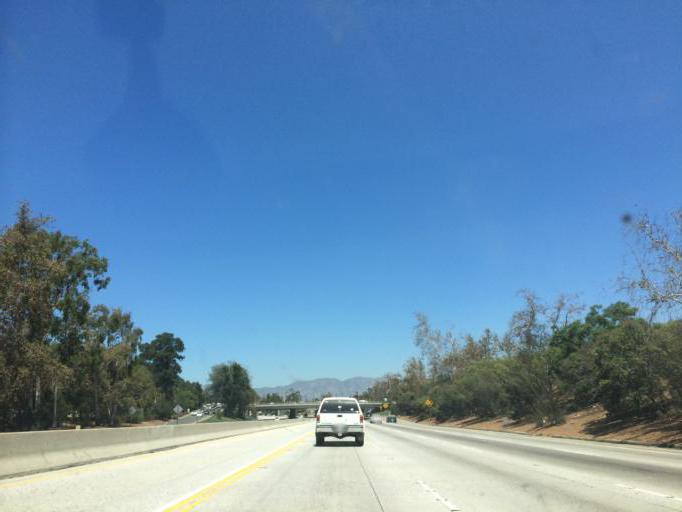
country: US
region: California
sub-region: Los Angeles County
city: North Hollywood
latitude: 34.1981
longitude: -118.4030
